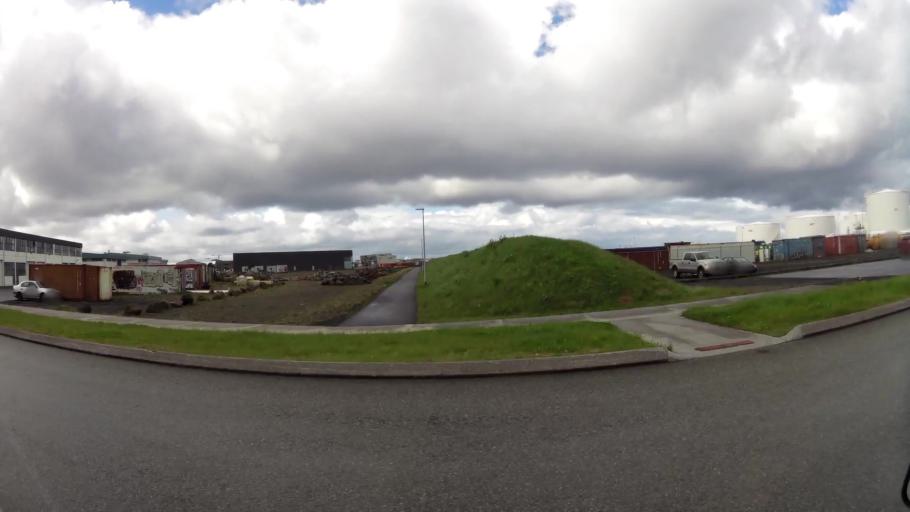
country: IS
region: Capital Region
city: Reykjavik
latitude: 64.1580
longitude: -21.9414
